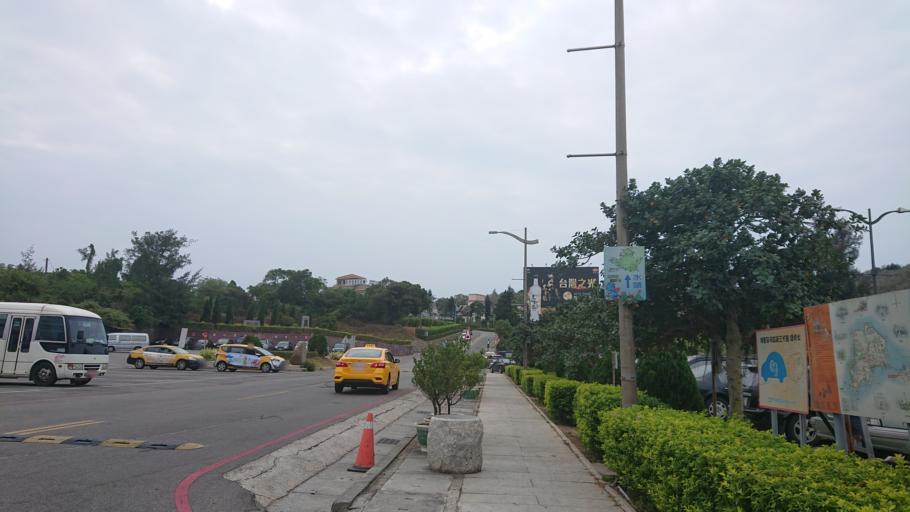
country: TW
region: Fukien
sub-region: Kinmen
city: Jincheng
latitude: 24.4151
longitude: 118.2864
